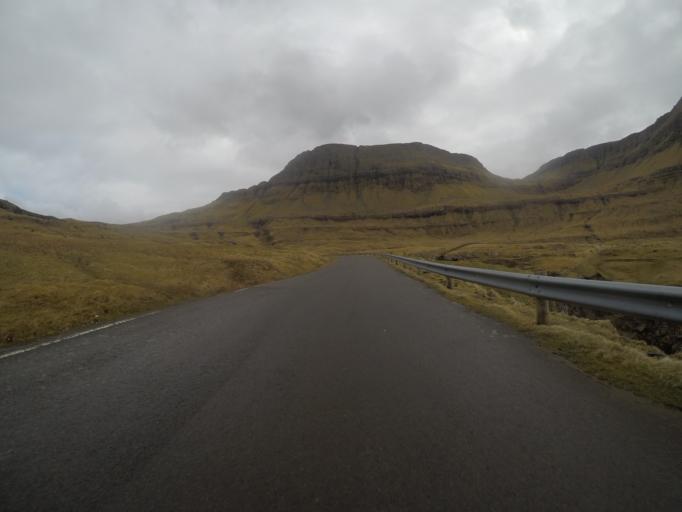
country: FO
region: Streymoy
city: Kollafjordhur
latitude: 62.0432
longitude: -6.9309
